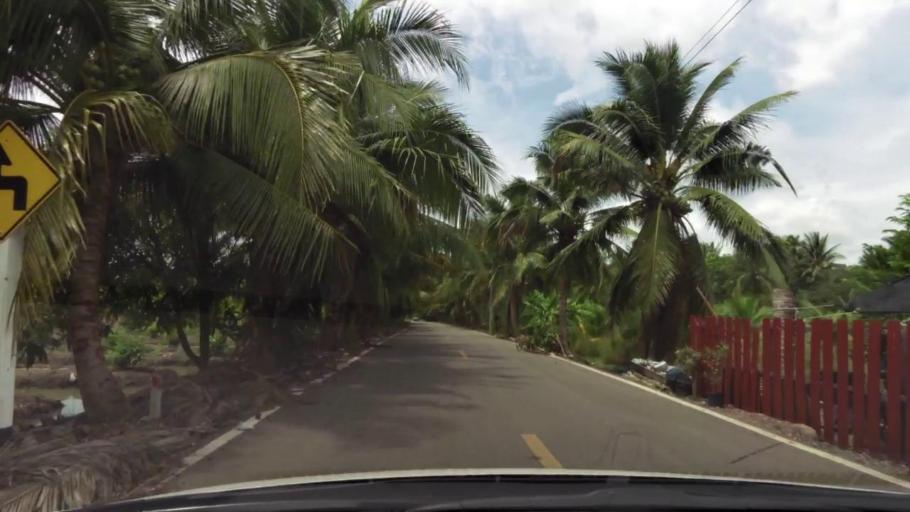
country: TH
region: Ratchaburi
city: Damnoen Saduak
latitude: 13.5215
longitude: 100.0135
